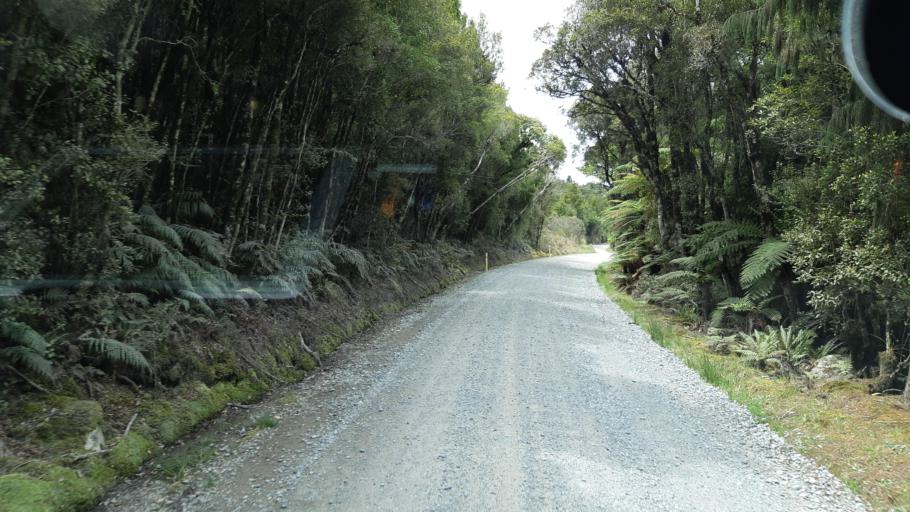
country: NZ
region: West Coast
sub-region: Westland District
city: Hokitika
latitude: -42.7289
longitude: 171.2290
